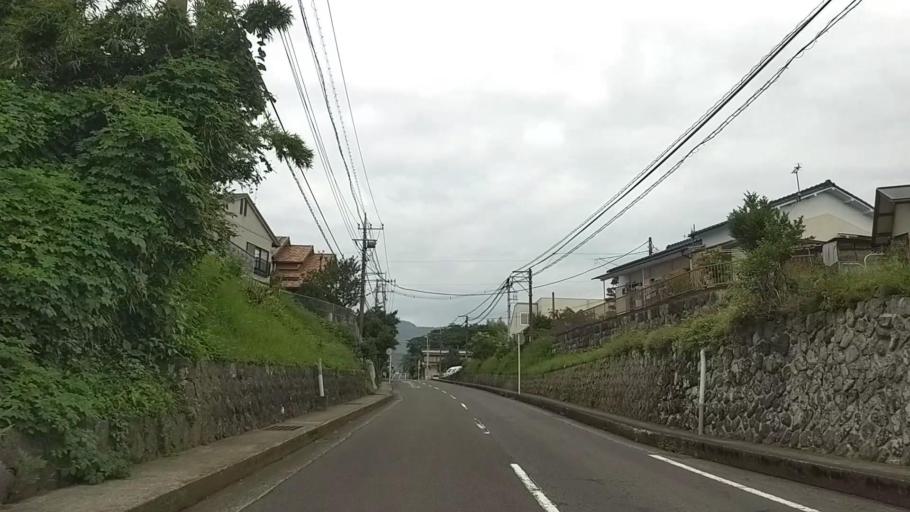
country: JP
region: Kanagawa
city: Odawara
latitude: 35.3255
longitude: 139.0937
